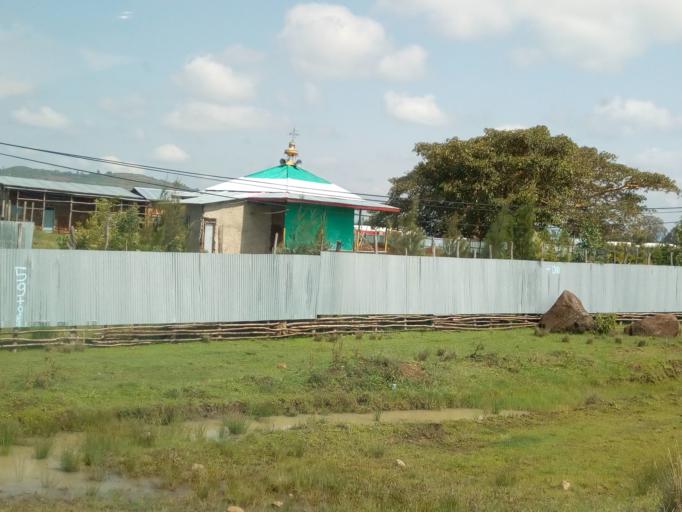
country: ET
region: Oromiya
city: Waliso
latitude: 8.5534
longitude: 37.9520
